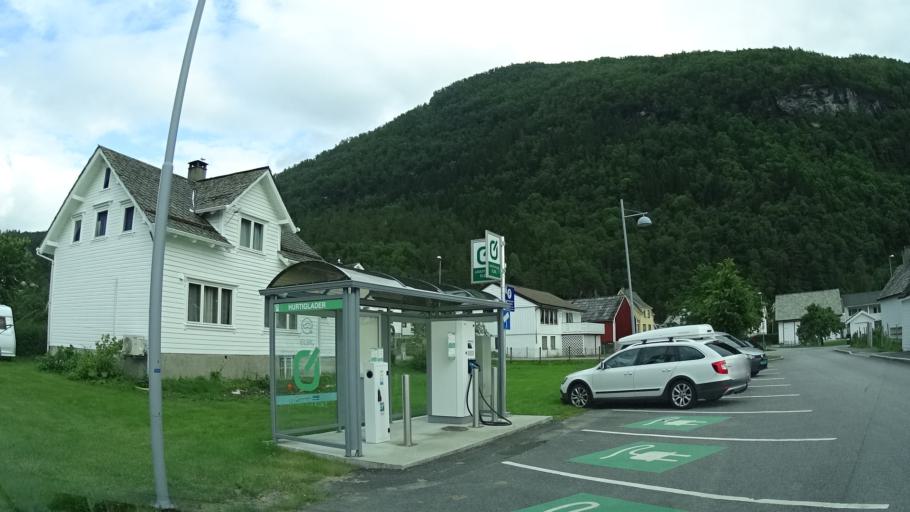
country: NO
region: Hordaland
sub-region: Jondal
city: Jondal
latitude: 60.2767
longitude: 6.2533
